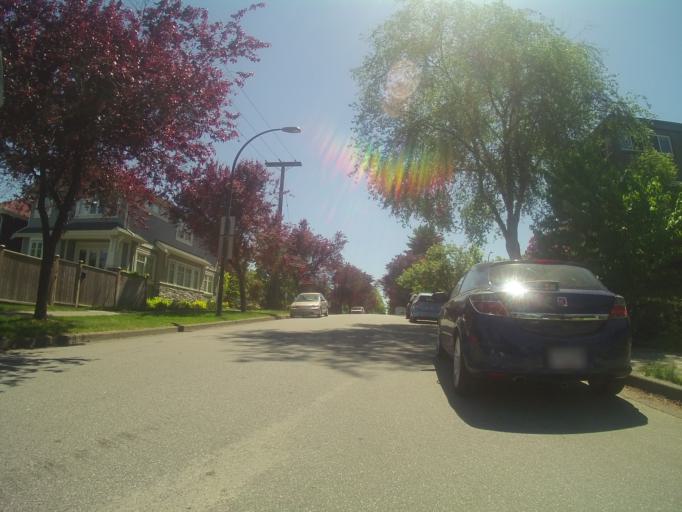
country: CA
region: British Columbia
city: Vancouver
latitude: 49.2368
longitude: -123.1055
